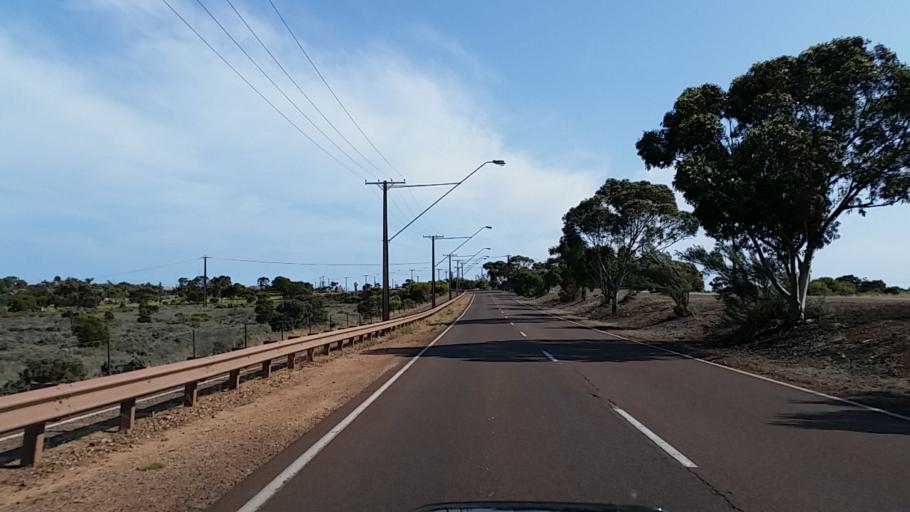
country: AU
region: South Australia
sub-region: Whyalla
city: Whyalla
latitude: -33.0215
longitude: 137.5740
